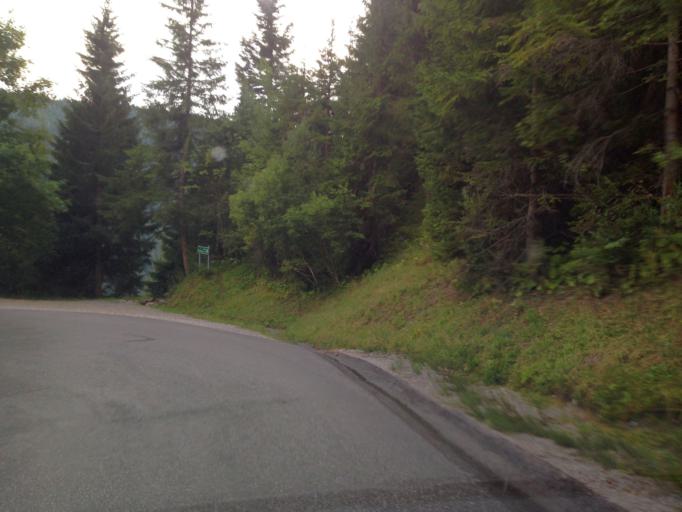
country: AT
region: Styria
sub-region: Politischer Bezirk Liezen
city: Schladming
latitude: 47.4311
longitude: 13.6068
